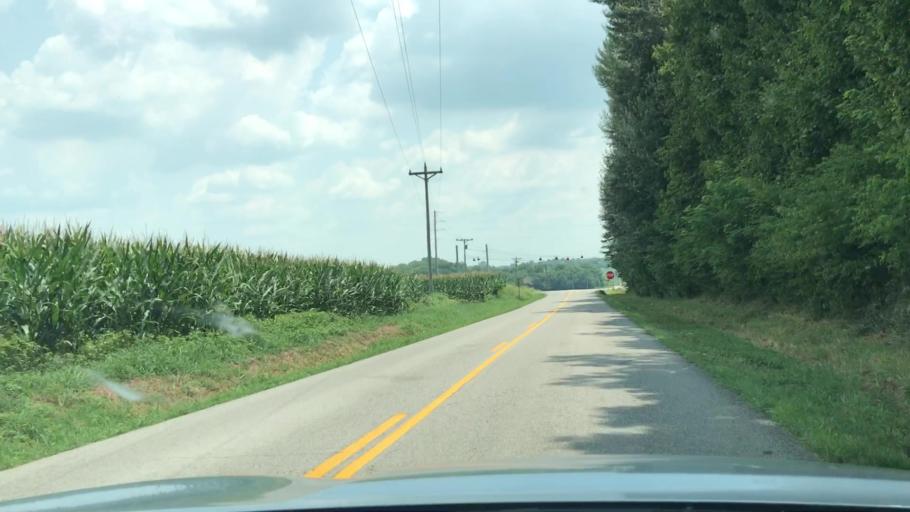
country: US
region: Kentucky
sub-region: Todd County
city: Elkton
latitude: 36.7259
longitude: -87.0880
